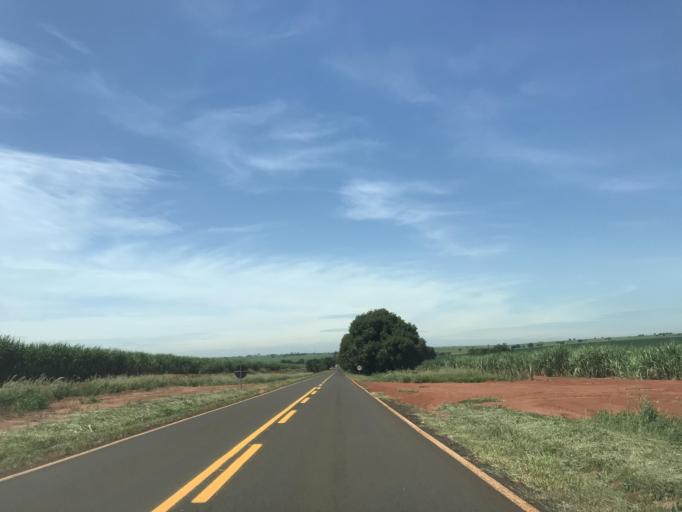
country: BR
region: Parana
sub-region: Terra Rica
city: Terra Rica
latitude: -22.8035
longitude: -52.6536
